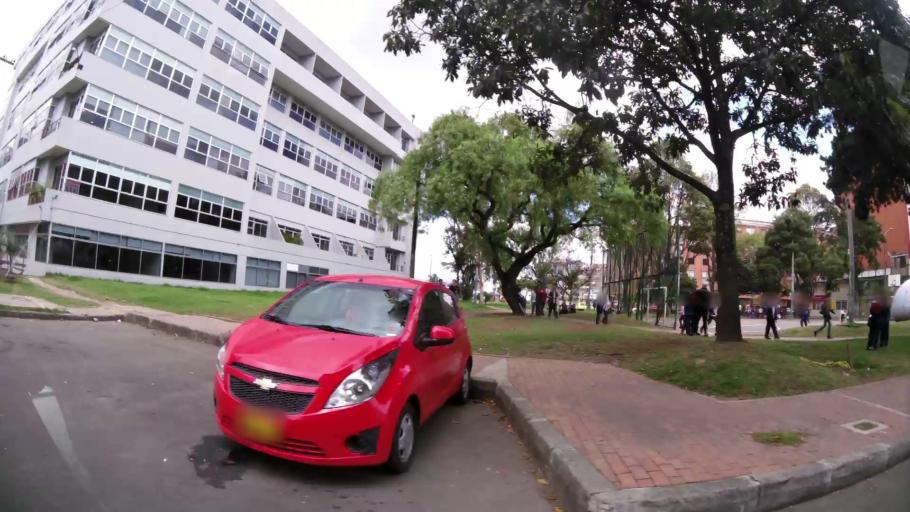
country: CO
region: Bogota D.C.
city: Bogota
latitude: 4.6342
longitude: -74.0959
